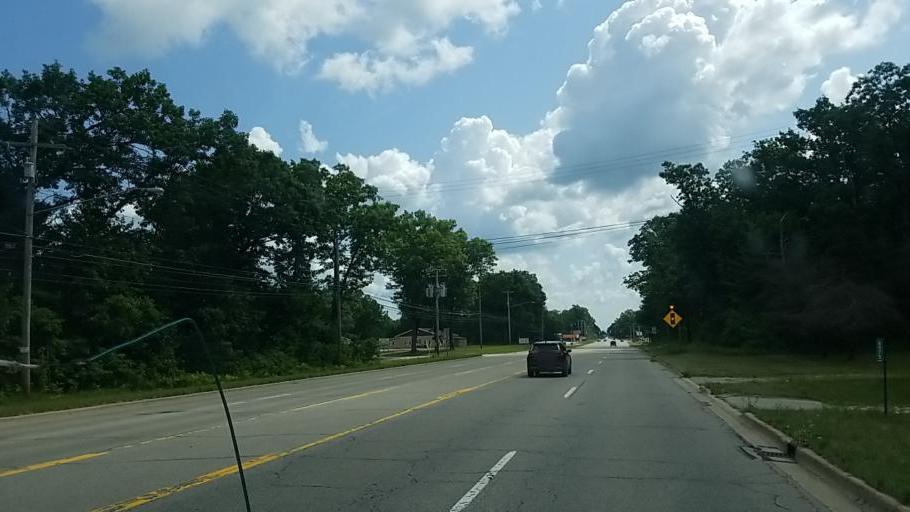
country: US
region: Michigan
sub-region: Muskegon County
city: Wolf Lake
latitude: 43.2349
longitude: -86.0731
